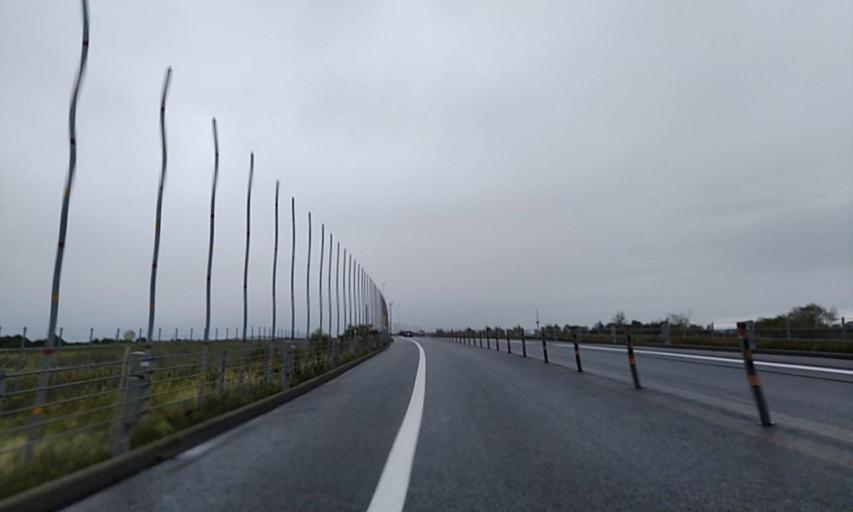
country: JP
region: Hokkaido
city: Kushiro
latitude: 43.0350
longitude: 144.3713
